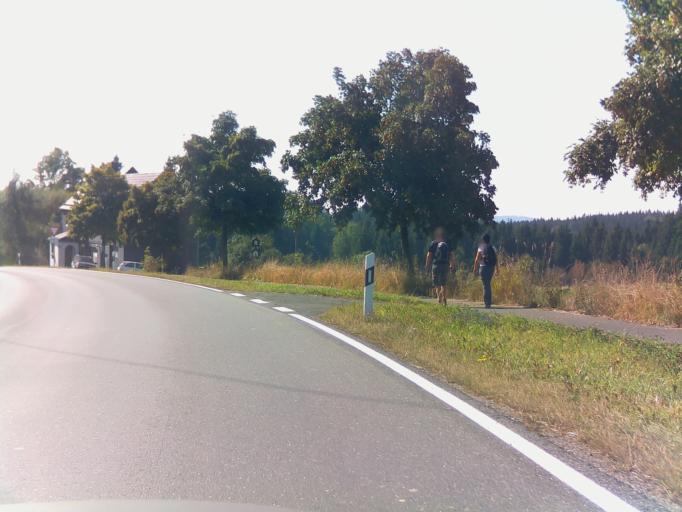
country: DE
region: Bavaria
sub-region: Upper Franconia
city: Reichenbach
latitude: 50.4510
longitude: 11.4091
